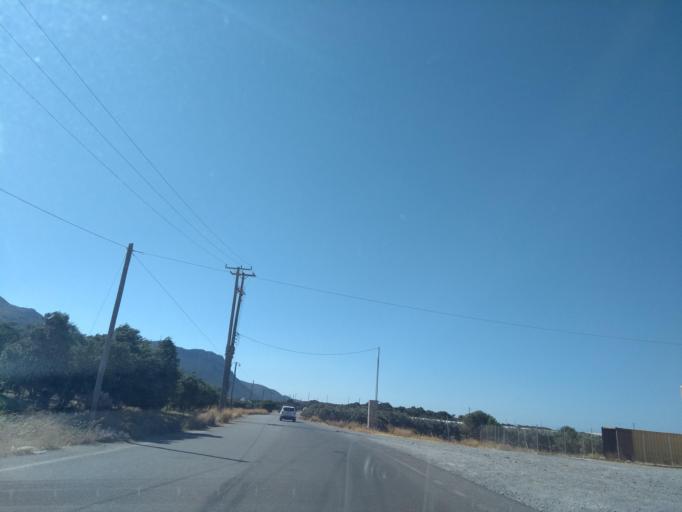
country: GR
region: Crete
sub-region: Nomos Chanias
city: Palaiochora
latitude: 35.2907
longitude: 23.5465
